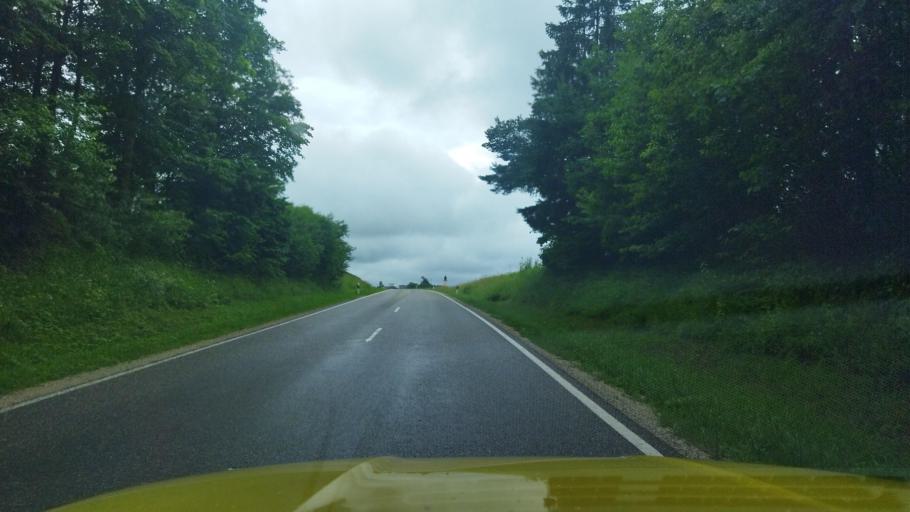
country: DE
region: Bavaria
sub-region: Upper Palatinate
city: Dietfurt
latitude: 48.9483
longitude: 11.5974
